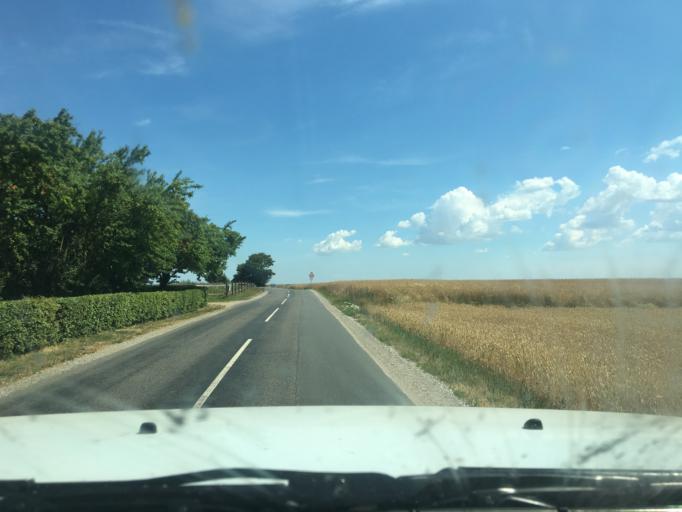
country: DK
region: Central Jutland
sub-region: Arhus Kommune
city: Trige
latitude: 56.3410
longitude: 10.2019
